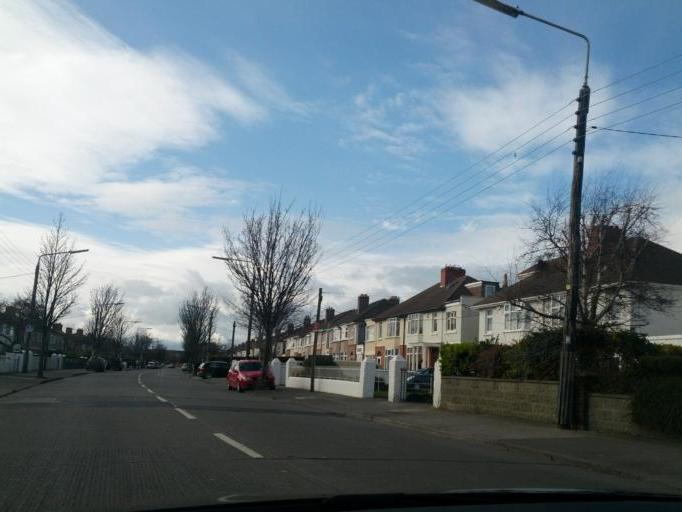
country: IE
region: Leinster
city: Marino
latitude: 53.3788
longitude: -6.2320
